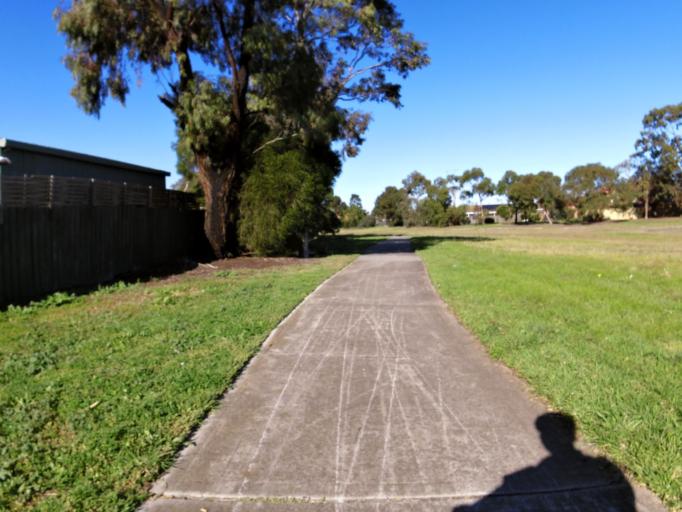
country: AU
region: Victoria
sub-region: Wyndham
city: Tarneit
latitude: -37.8743
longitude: 144.6733
